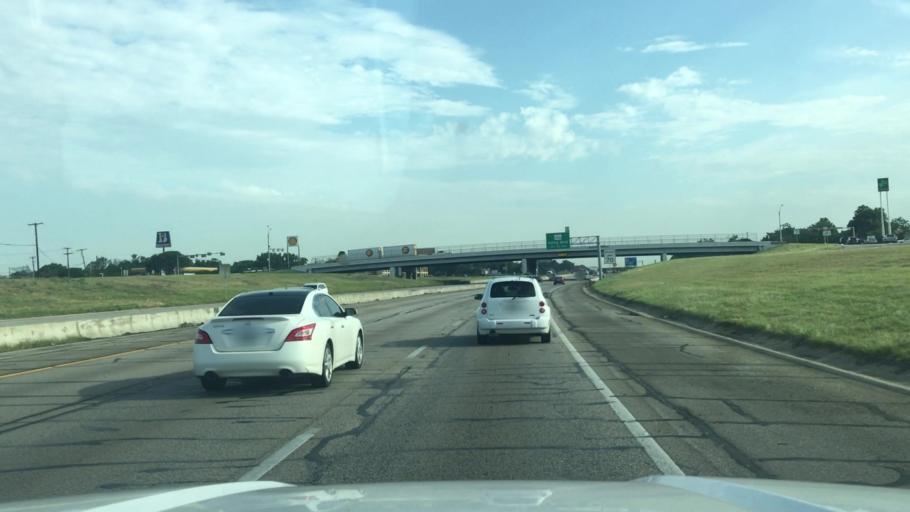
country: US
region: Texas
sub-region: Dallas County
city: Irving
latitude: 32.7991
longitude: -96.9215
